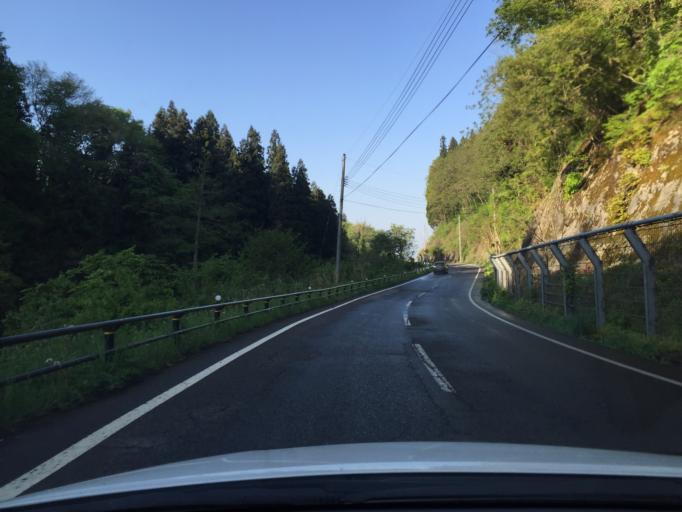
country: JP
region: Fukushima
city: Kitakata
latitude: 37.6579
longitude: 139.9464
